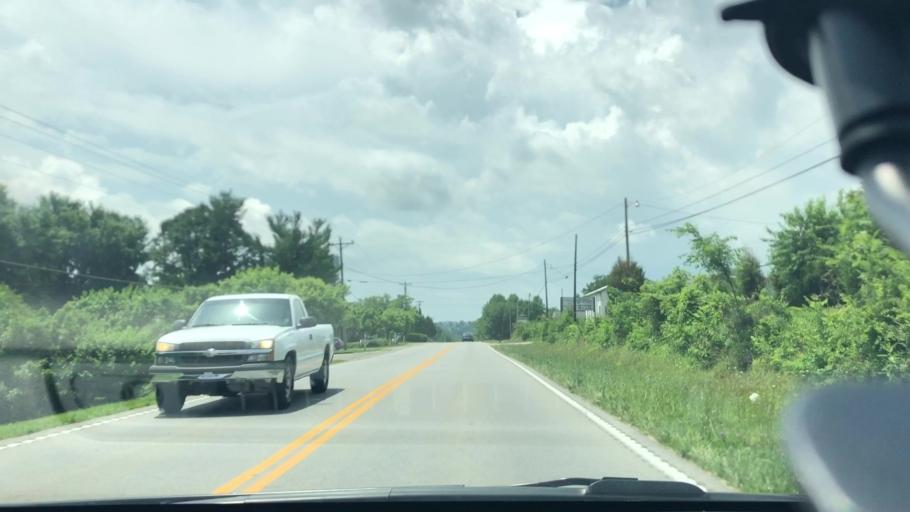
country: US
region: Kentucky
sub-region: Pulaski County
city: Somerset
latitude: 37.0605
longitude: -84.6756
